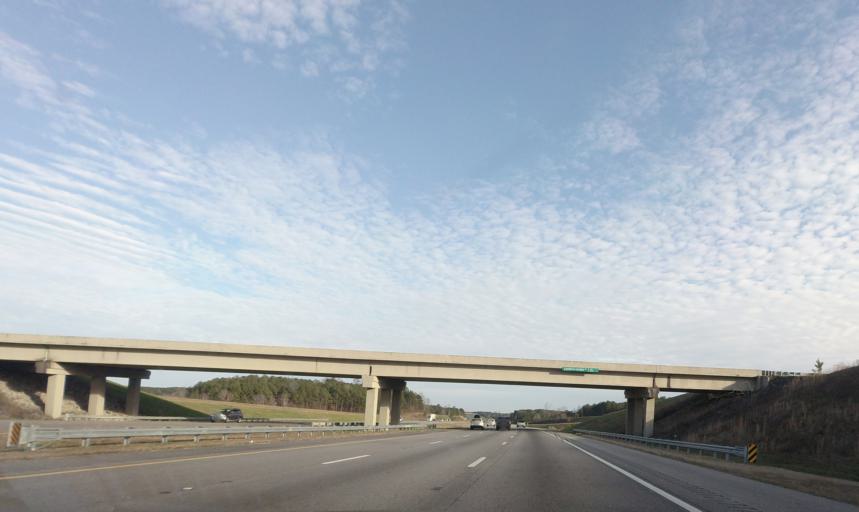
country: US
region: Alabama
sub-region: Walker County
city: Cordova
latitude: 33.7193
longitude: -87.1813
